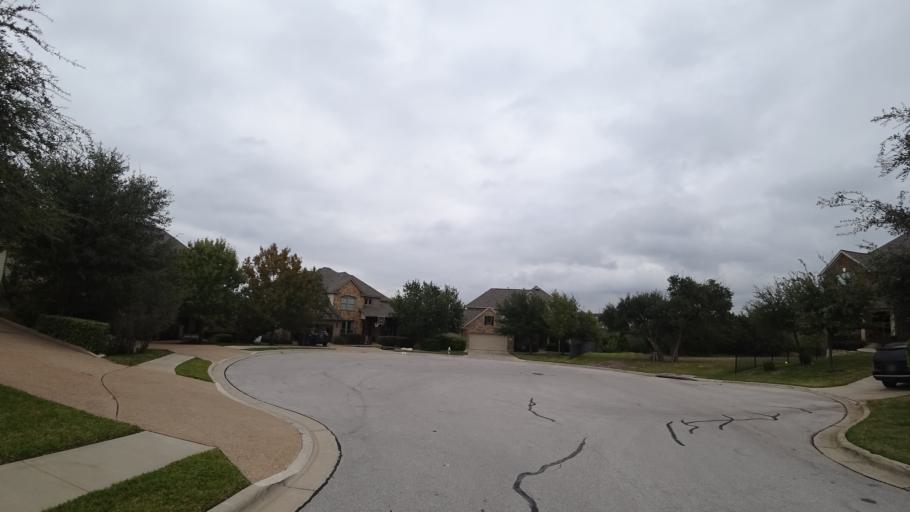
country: US
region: Texas
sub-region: Travis County
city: Hudson Bend
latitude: 30.3601
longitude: -97.9065
